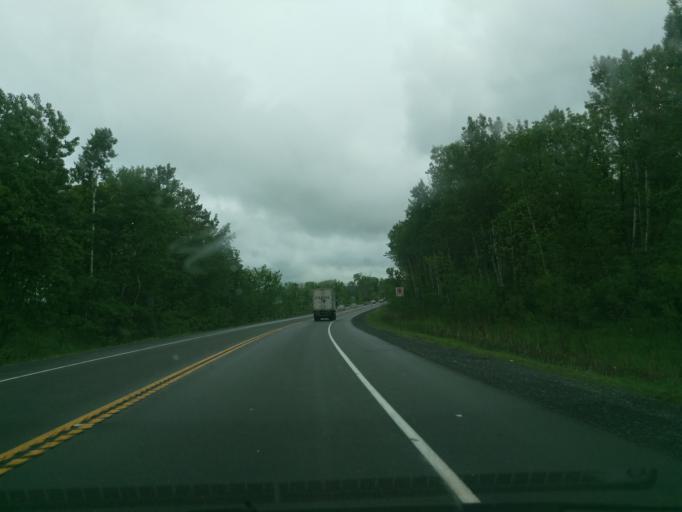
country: CA
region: Ontario
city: Clarence-Rockland
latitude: 45.5012
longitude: -75.4768
